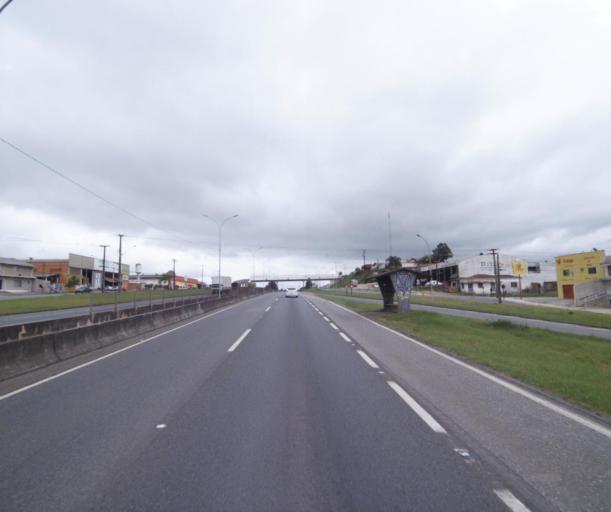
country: BR
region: Parana
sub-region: Quatro Barras
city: Quatro Barras
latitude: -25.3676
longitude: -49.1040
